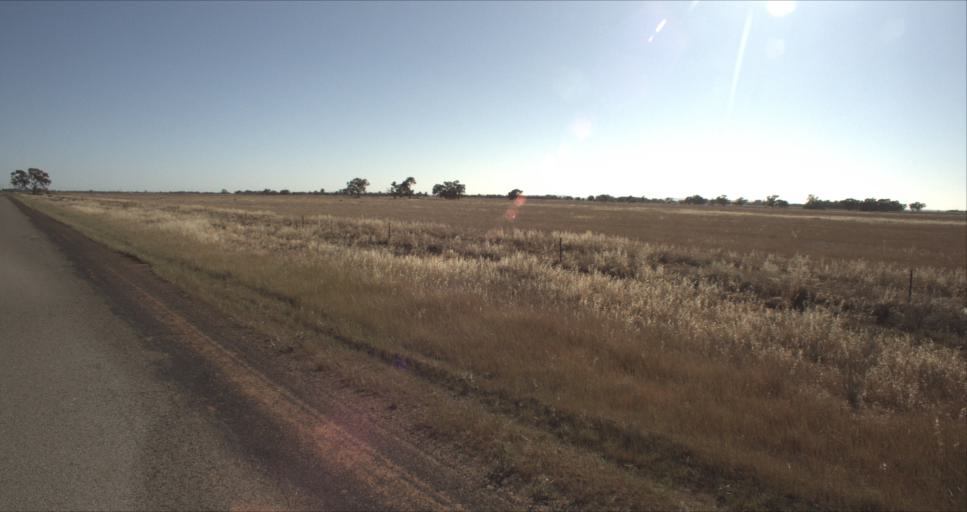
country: AU
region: New South Wales
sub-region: Leeton
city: Leeton
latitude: -34.5598
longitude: 146.2656
